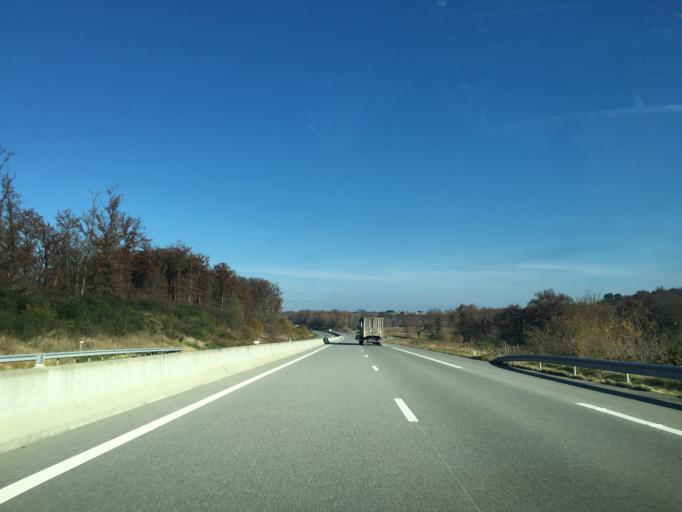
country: FR
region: Midi-Pyrenees
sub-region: Departement du Gers
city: Barcelonne-du-Gers
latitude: 43.6533
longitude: -0.2906
